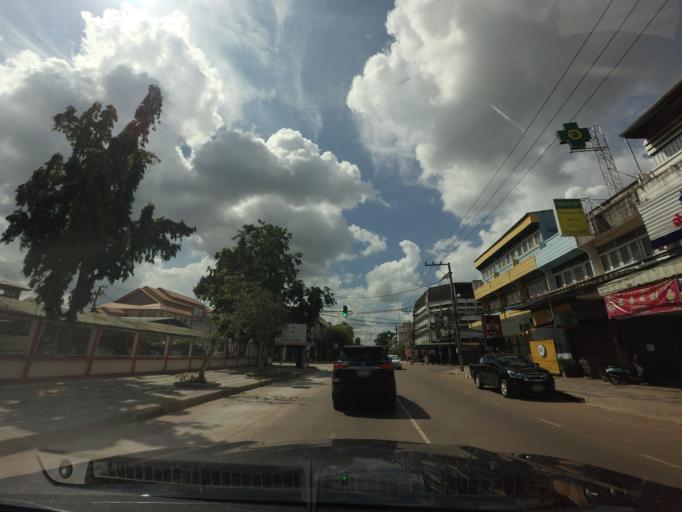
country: TH
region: Changwat Udon Thani
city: Udon Thani
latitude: 17.4056
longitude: 102.7856
